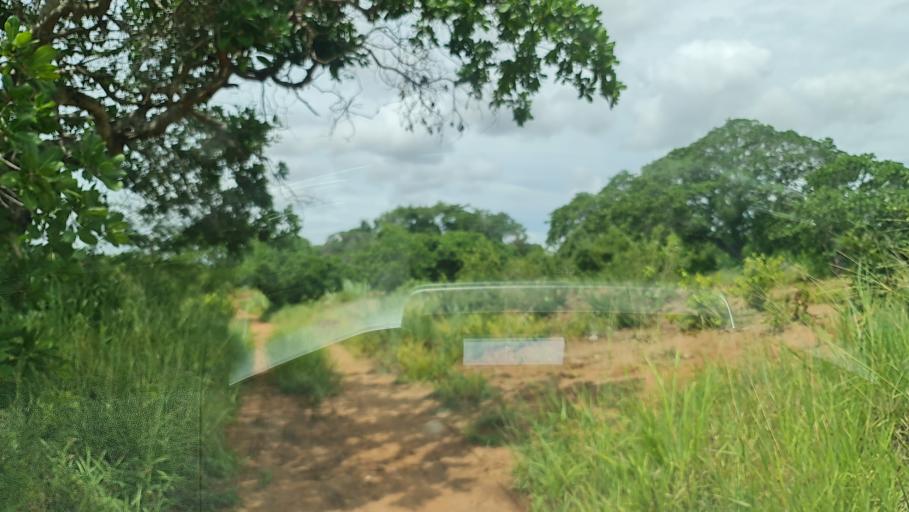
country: MZ
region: Nampula
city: Nacala
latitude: -14.7873
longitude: 39.9747
